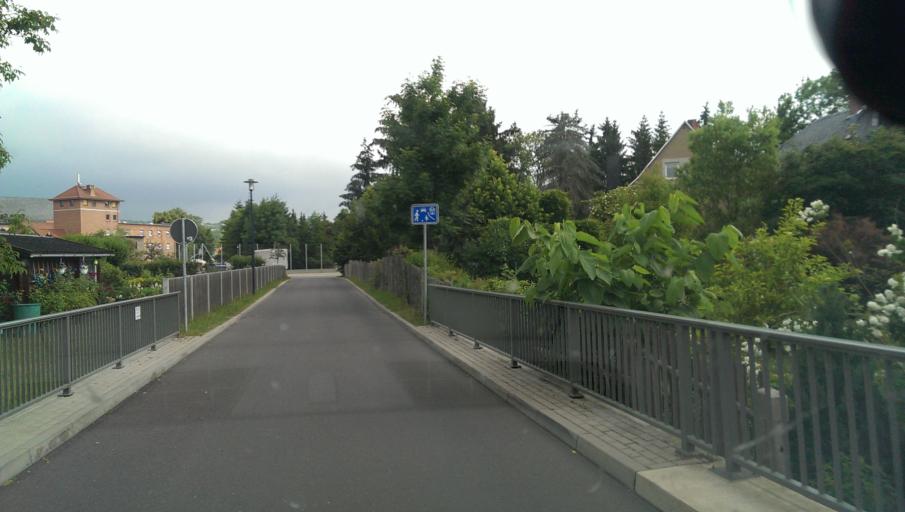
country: DE
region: Thuringia
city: Bad Berka
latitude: 50.8986
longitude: 11.2857
